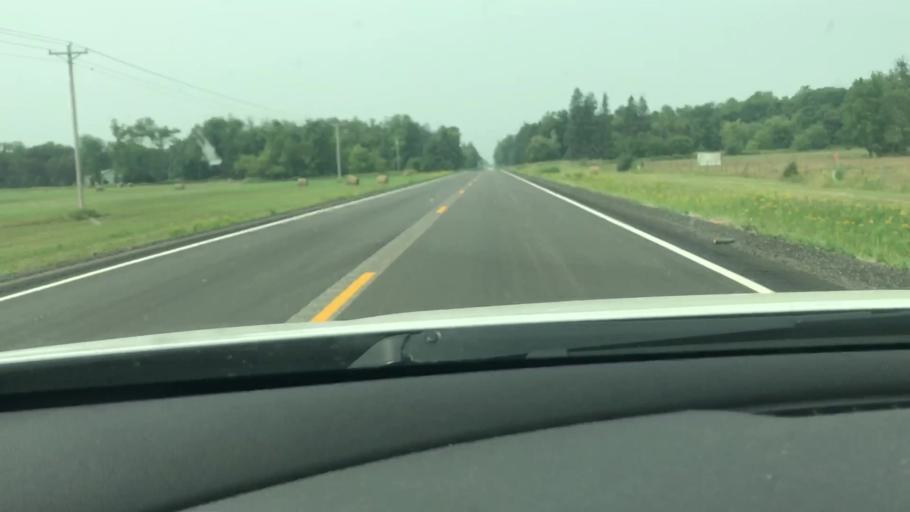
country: US
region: Minnesota
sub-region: Itasca County
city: Cohasset
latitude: 47.3555
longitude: -93.8505
